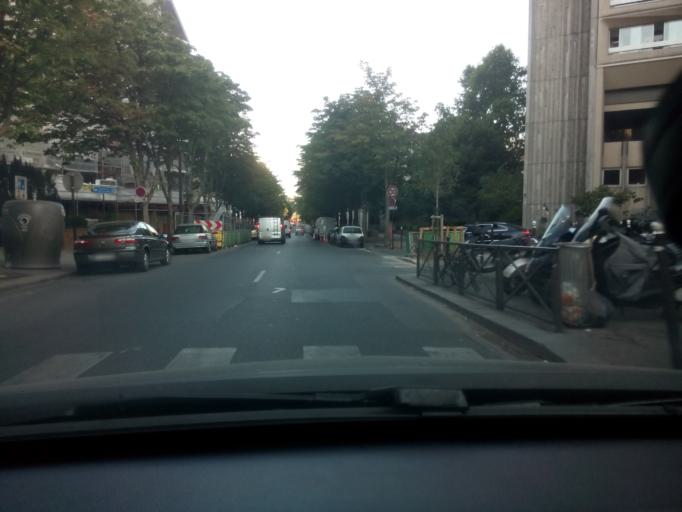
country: FR
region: Ile-de-France
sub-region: Departement du Val-de-Marne
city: Le Kremlin-Bicetre
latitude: 48.8242
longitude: 2.3641
